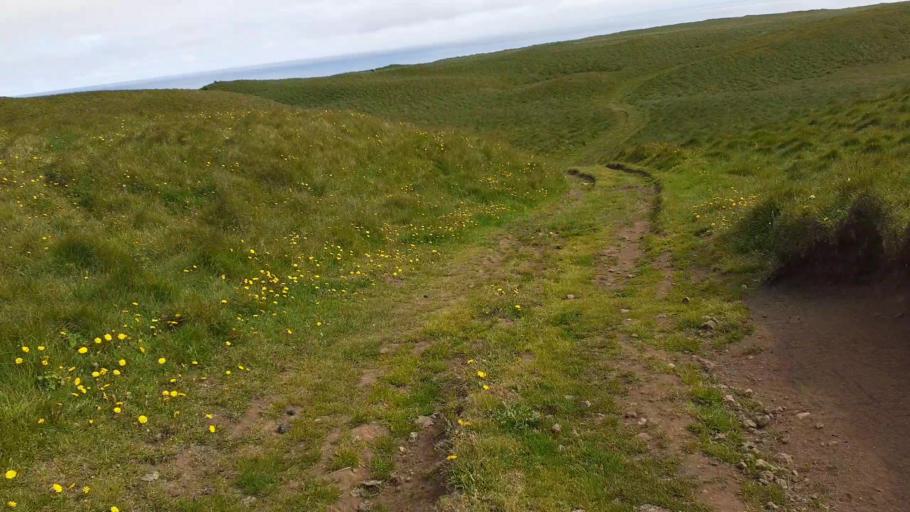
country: IS
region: Northeast
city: Dalvik
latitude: 66.5436
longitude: -17.9858
